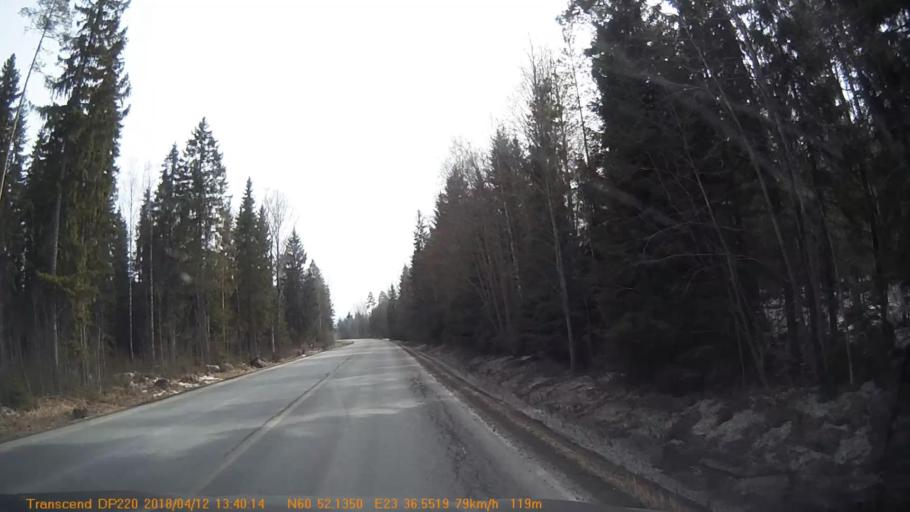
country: FI
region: Haeme
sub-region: Forssa
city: Forssa
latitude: 60.8682
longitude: 23.6097
